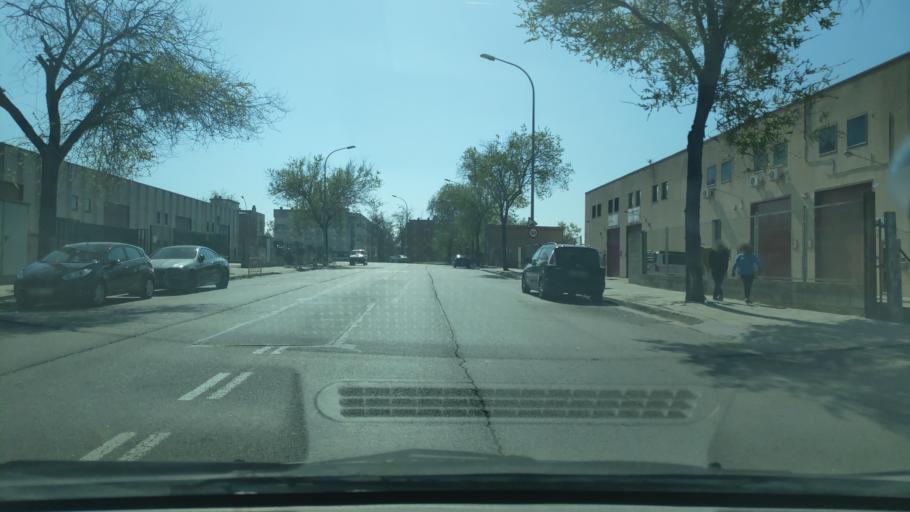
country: ES
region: Catalonia
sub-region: Provincia de Barcelona
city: Sabadell
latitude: 41.5431
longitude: 2.1297
